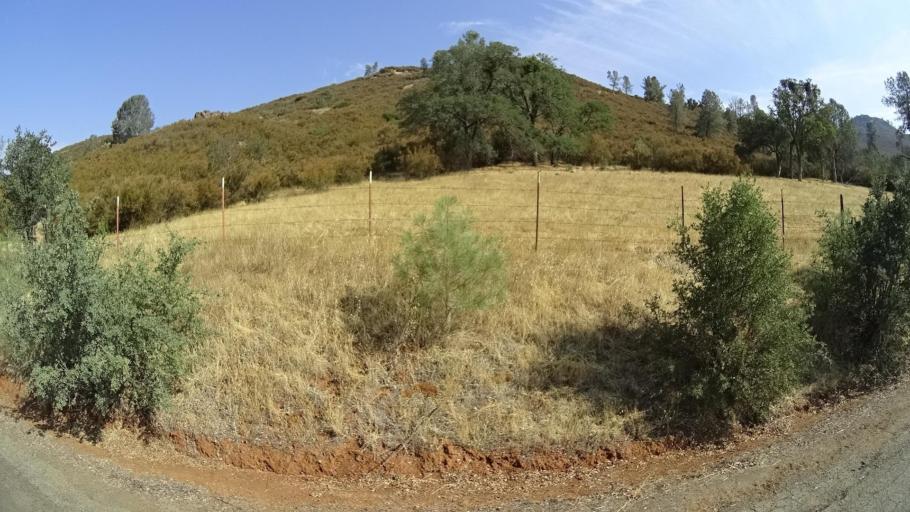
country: US
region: California
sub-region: Tuolumne County
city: Tuolumne City
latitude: 37.7215
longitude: -120.2752
